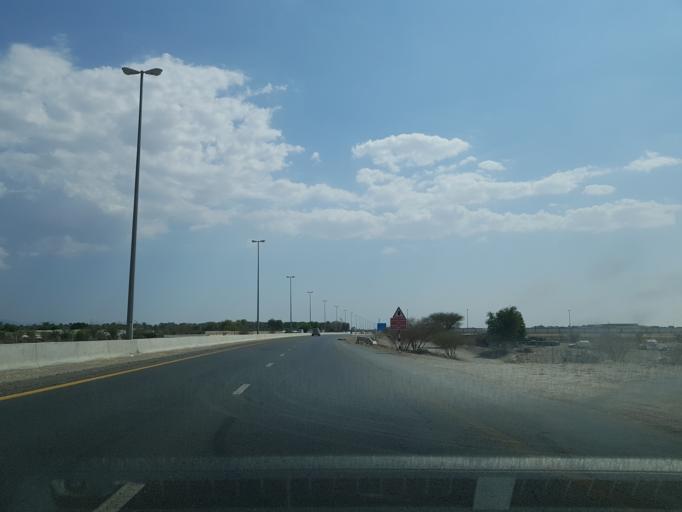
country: AE
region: Ash Shariqah
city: Adh Dhayd
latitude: 25.2389
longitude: 55.9160
